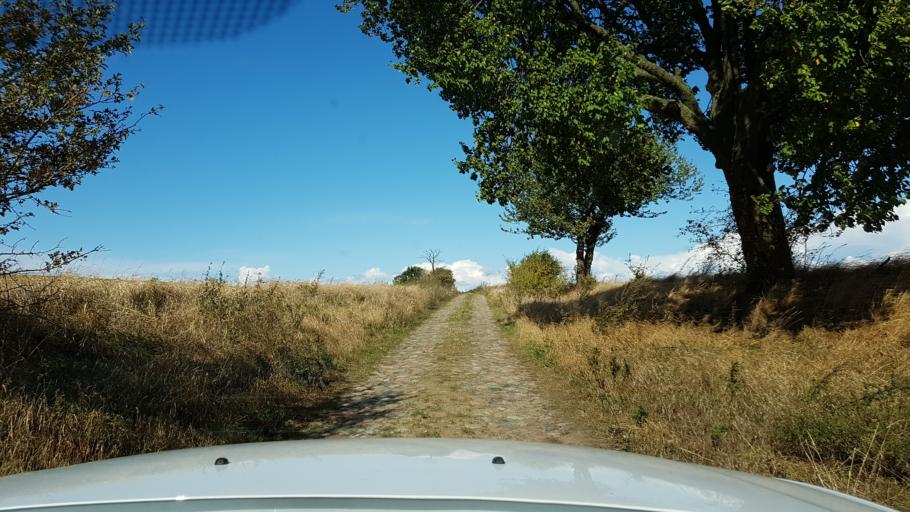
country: PL
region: West Pomeranian Voivodeship
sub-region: Powiat gryfinski
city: Banie
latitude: 53.1363
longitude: 14.6446
